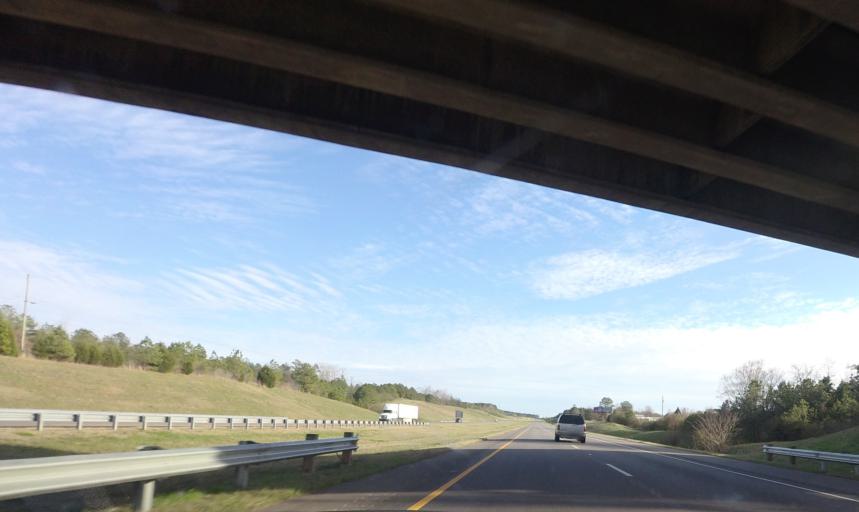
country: US
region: Alabama
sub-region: Walker County
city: Jasper
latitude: 33.8399
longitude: -87.3312
